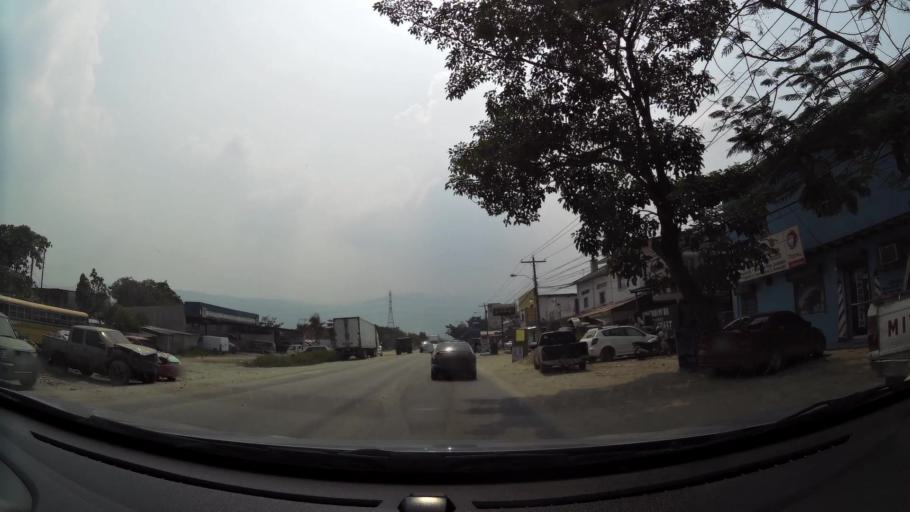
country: HN
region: Cortes
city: San Pedro Sula
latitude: 15.4715
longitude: -87.9998
